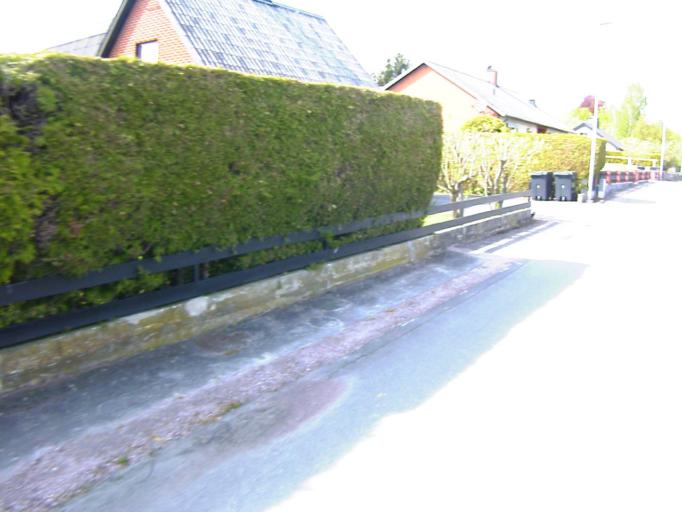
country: SE
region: Skane
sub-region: Kristianstads Kommun
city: Fjalkinge
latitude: 56.0985
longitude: 14.2483
